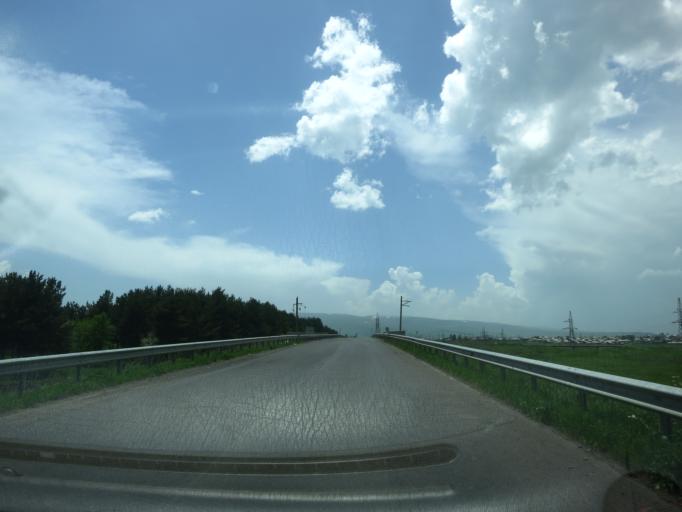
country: GE
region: Samtskhe-Javakheti
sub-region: Ninotsminda
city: Ninotsminda
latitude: 41.2749
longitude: 43.6112
